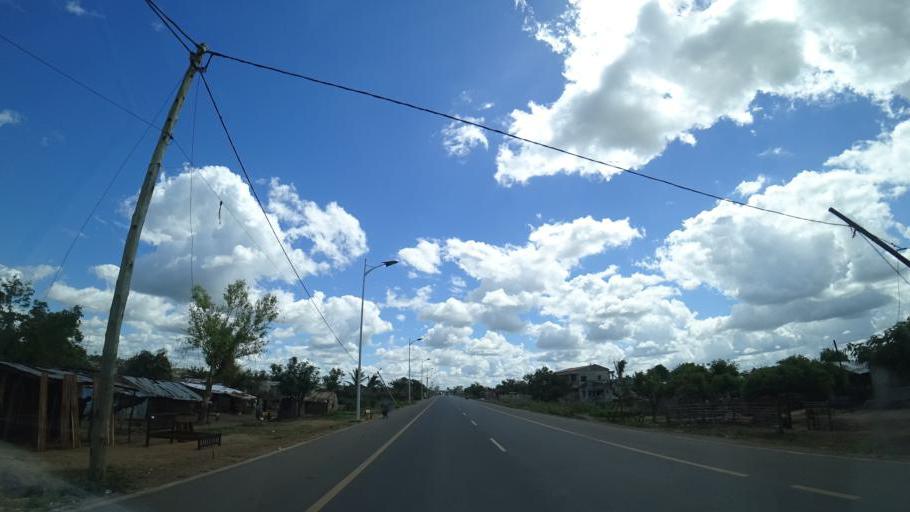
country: MZ
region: Sofala
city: Dondo
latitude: -19.2740
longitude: 34.2133
